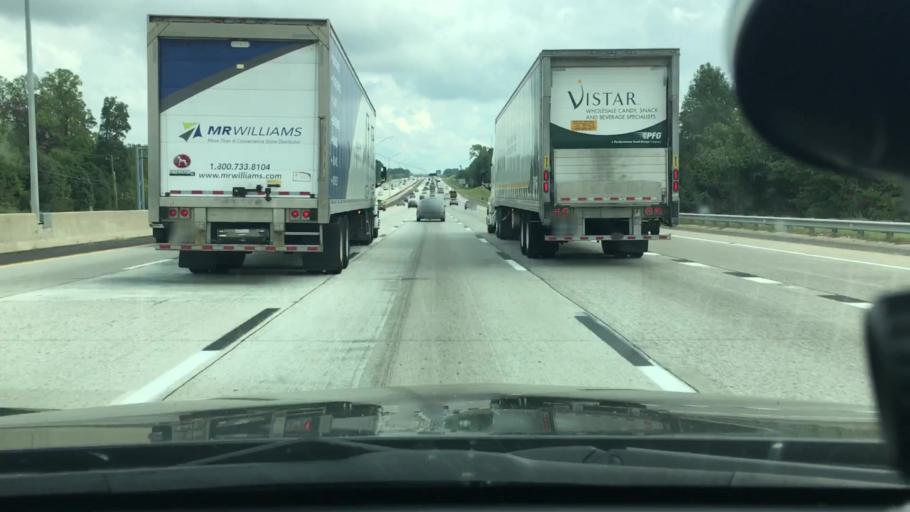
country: US
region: North Carolina
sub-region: Guilford County
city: Oak Ridge
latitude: 36.0908
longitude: -79.9927
